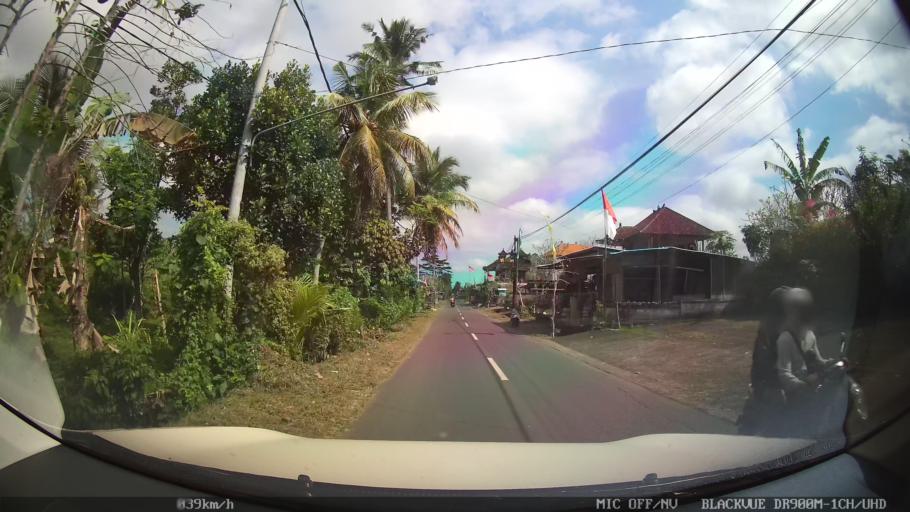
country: ID
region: Bali
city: Banjar Pesalakan
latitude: -8.5104
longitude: 115.3128
